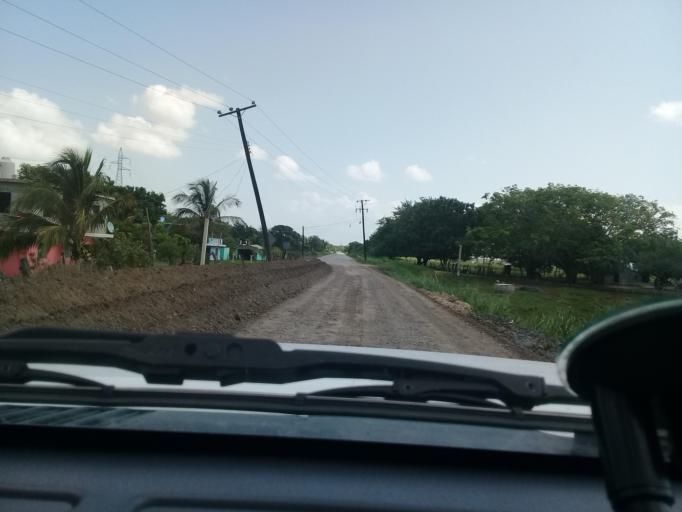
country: MX
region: Veracruz
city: Moralillo
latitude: 22.1802
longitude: -97.9473
